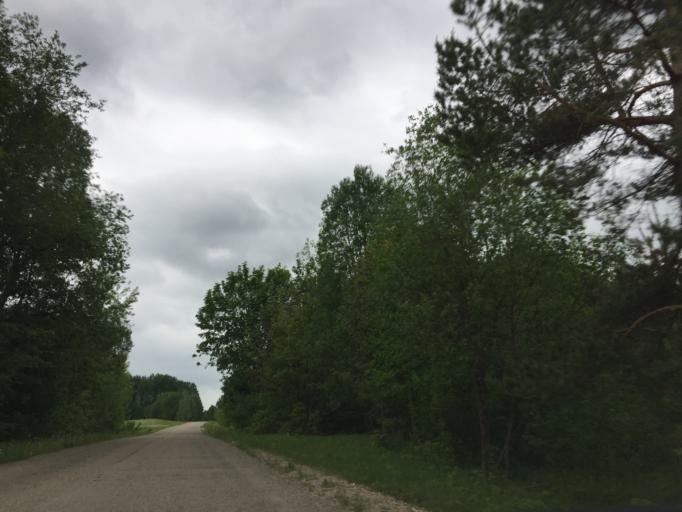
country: LV
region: Aglona
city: Aglona
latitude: 56.0812
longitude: 26.9169
